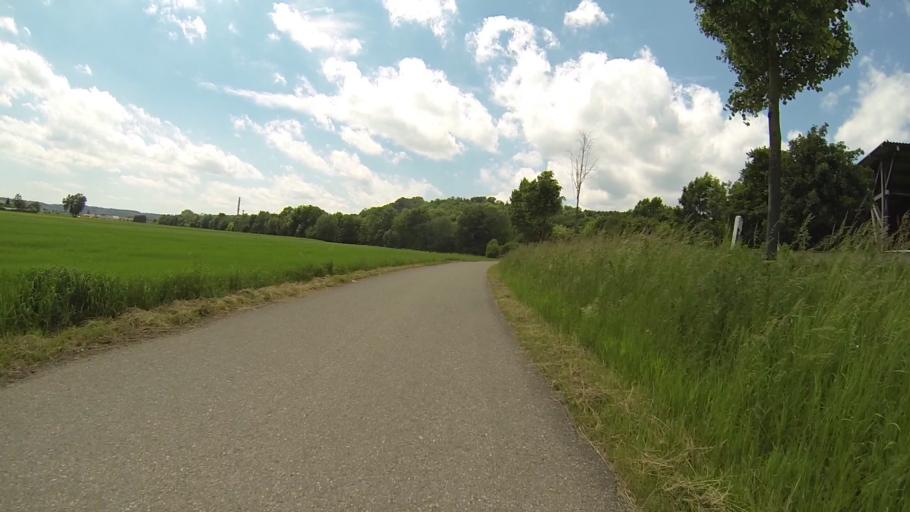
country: DE
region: Baden-Wuerttemberg
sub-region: Regierungsbezirk Stuttgart
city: Bolheim
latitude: 48.6442
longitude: 10.1594
